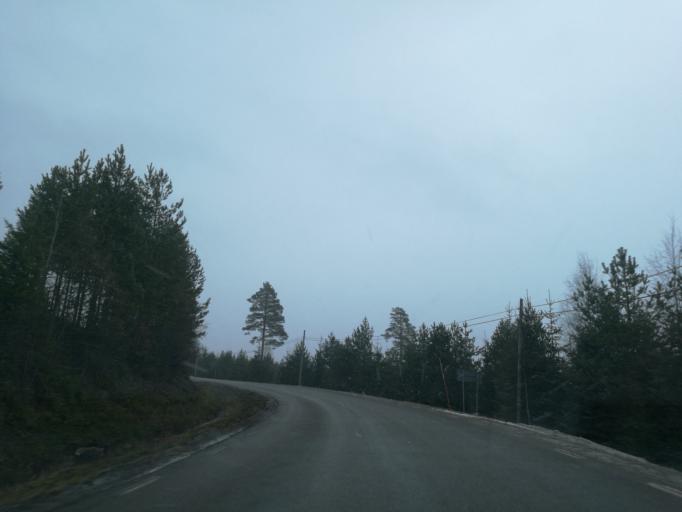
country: NO
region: Hedmark
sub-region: Asnes
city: Flisa
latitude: 60.6950
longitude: 12.5467
